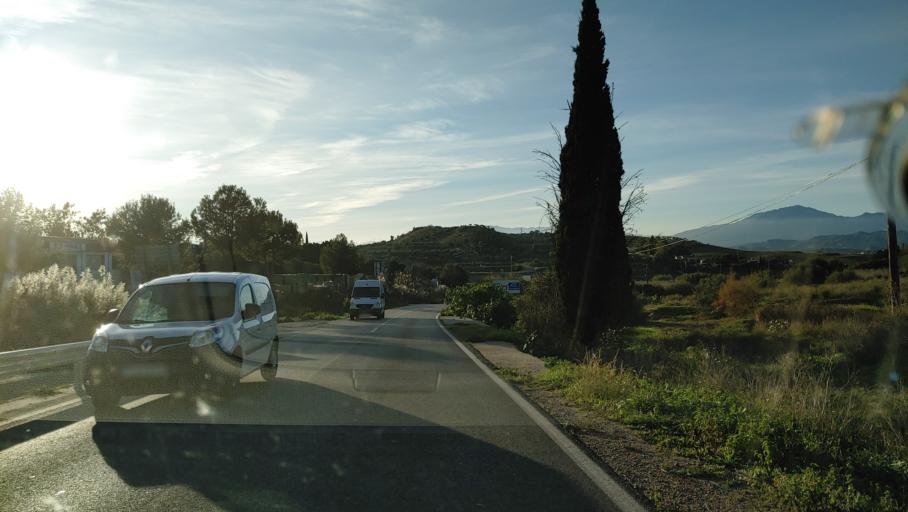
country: ES
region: Andalusia
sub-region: Provincia de Malaga
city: Cartama
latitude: 36.7122
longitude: -4.6401
